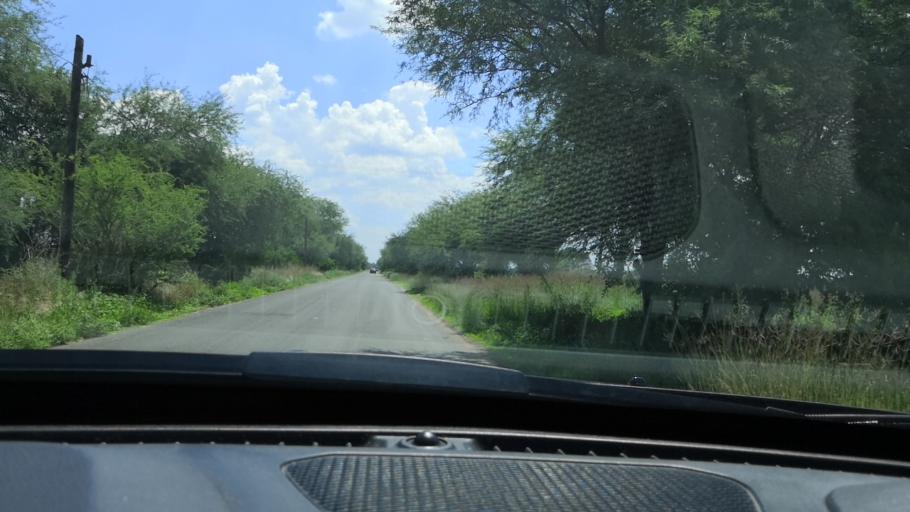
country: MX
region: Guanajuato
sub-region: Leon
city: Plan Guanajuato (La Sandia)
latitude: 20.9416
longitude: -101.6265
